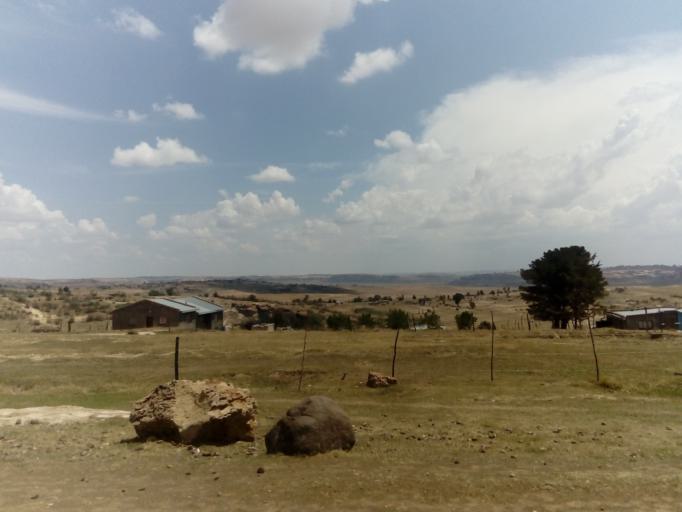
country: LS
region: Berea
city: Teyateyaneng
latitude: -29.1994
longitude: 27.7693
